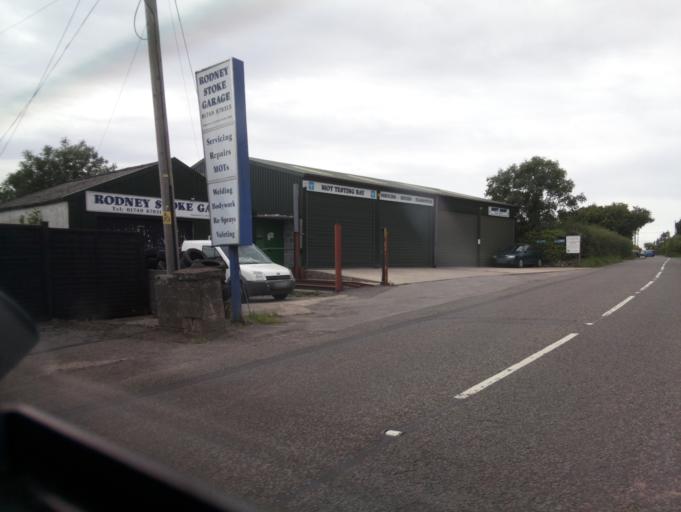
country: GB
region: England
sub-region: Somerset
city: Bradley Cross
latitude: 51.2502
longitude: -2.7416
